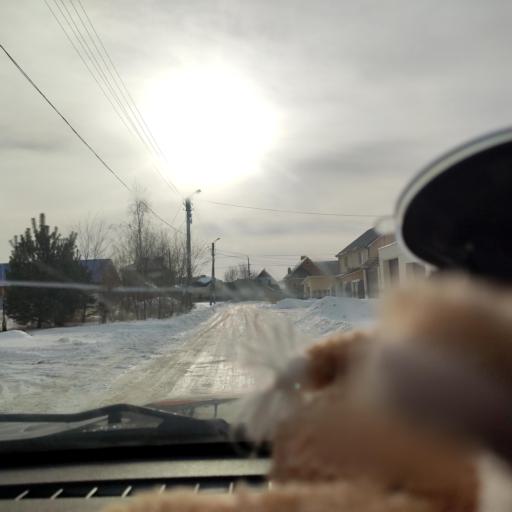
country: RU
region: Samara
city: Tol'yatti
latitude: 53.5565
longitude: 49.3724
